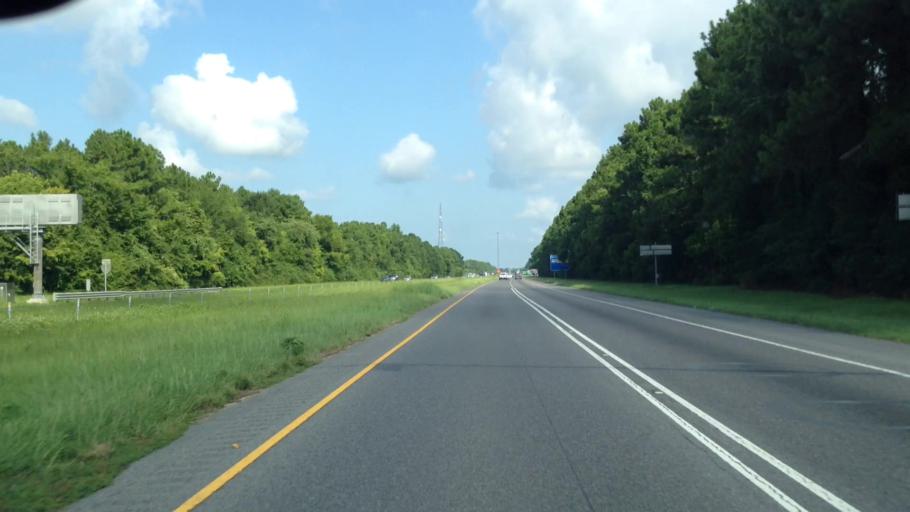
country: US
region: Louisiana
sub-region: Saint John the Baptist Parish
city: Laplace
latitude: 30.0969
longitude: -90.4708
